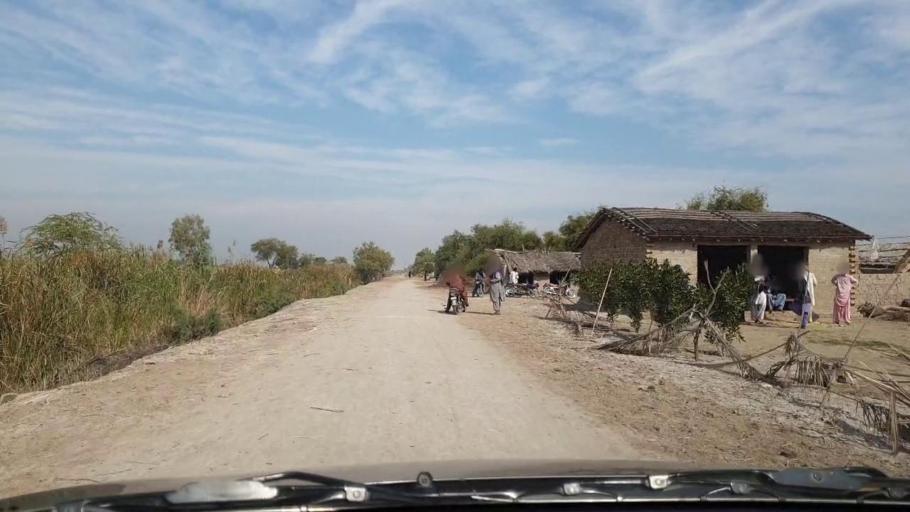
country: PK
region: Sindh
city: Jam Sahib
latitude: 26.2728
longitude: 68.7143
